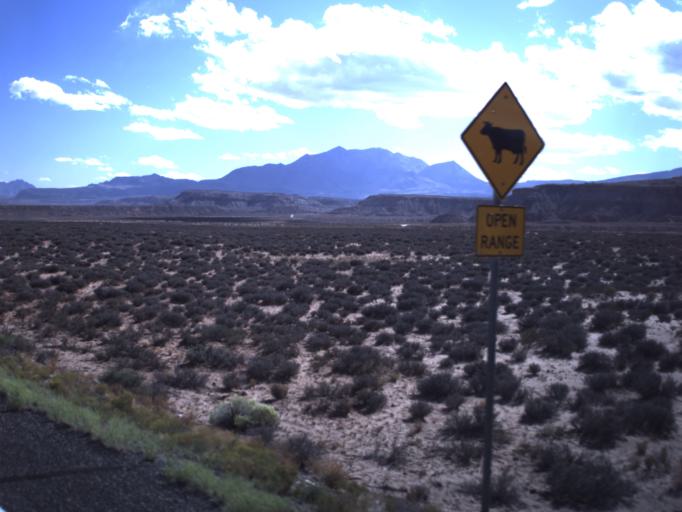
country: US
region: Utah
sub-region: Wayne County
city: Loa
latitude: 38.0952
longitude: -110.6205
